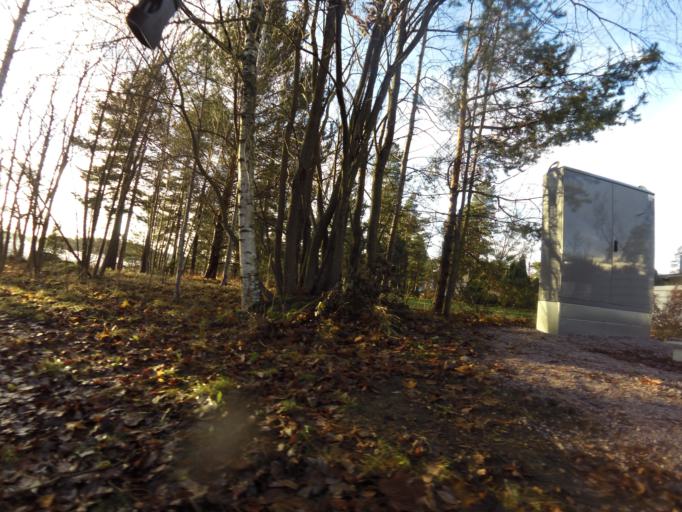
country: FI
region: Uusimaa
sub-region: Helsinki
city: Koukkuniemi
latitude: 60.1546
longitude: 24.7686
